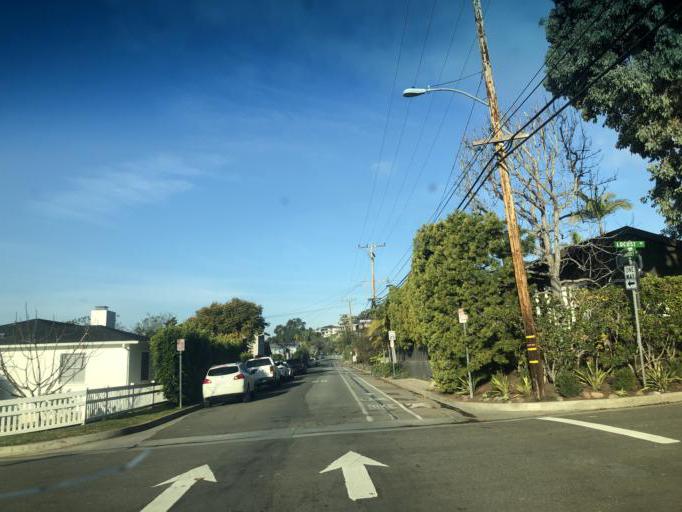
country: US
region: California
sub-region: Orange County
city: Laguna Beach
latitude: 33.5473
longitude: -117.7900
